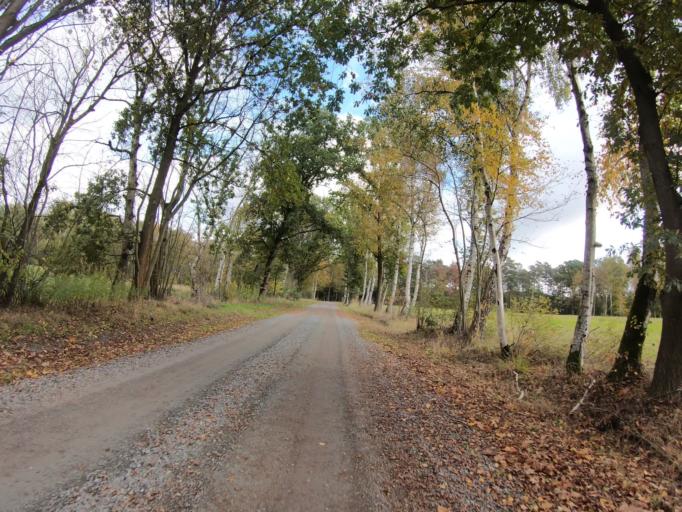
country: DE
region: Lower Saxony
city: Wesendorf
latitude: 52.5662
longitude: 10.5627
